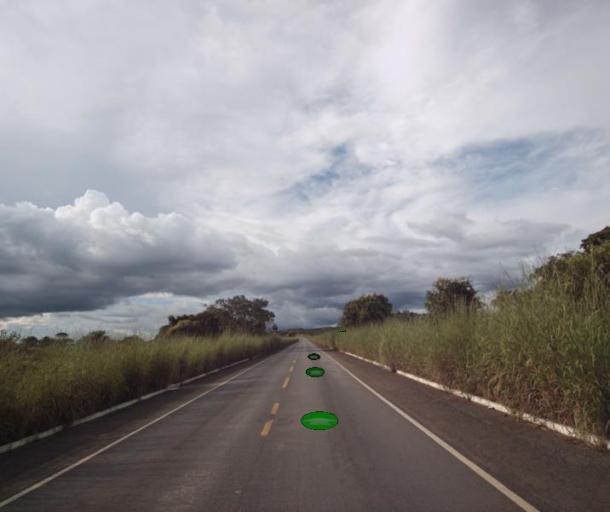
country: BR
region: Goias
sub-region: Niquelandia
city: Niquelandia
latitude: -14.6384
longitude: -48.5898
